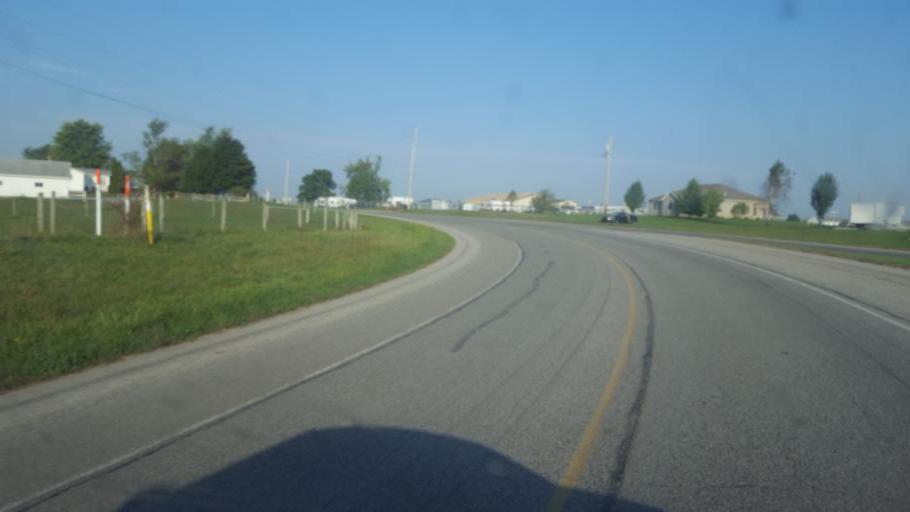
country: US
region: Indiana
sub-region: LaGrange County
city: Topeka
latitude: 41.6547
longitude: -85.5417
